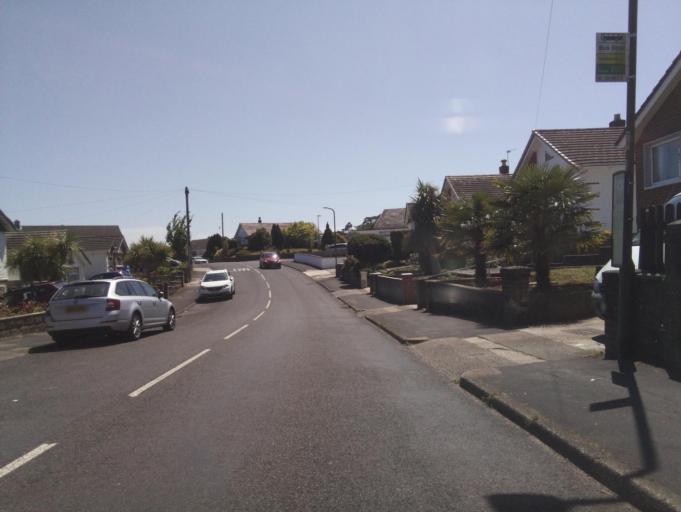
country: GB
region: England
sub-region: Borough of Torbay
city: Paignton
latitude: 50.4265
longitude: -3.5745
